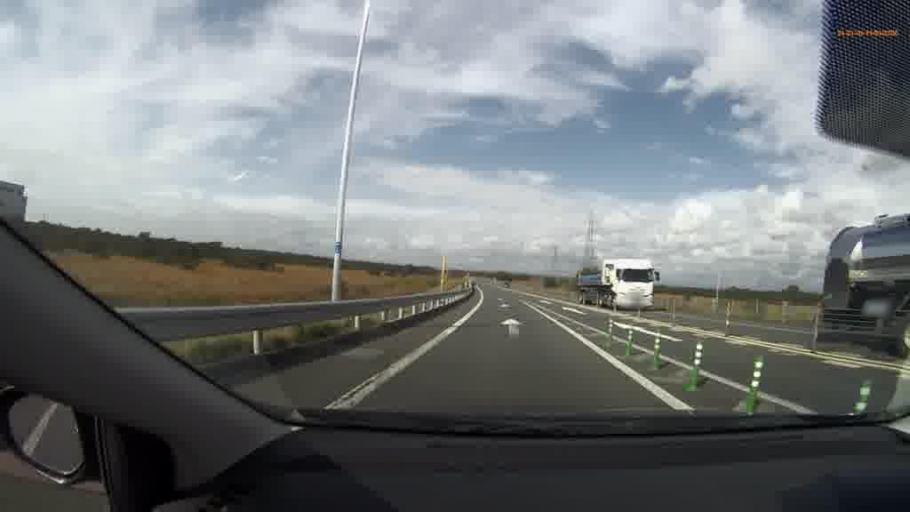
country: JP
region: Hokkaido
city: Kushiro
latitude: 43.0304
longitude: 144.4010
